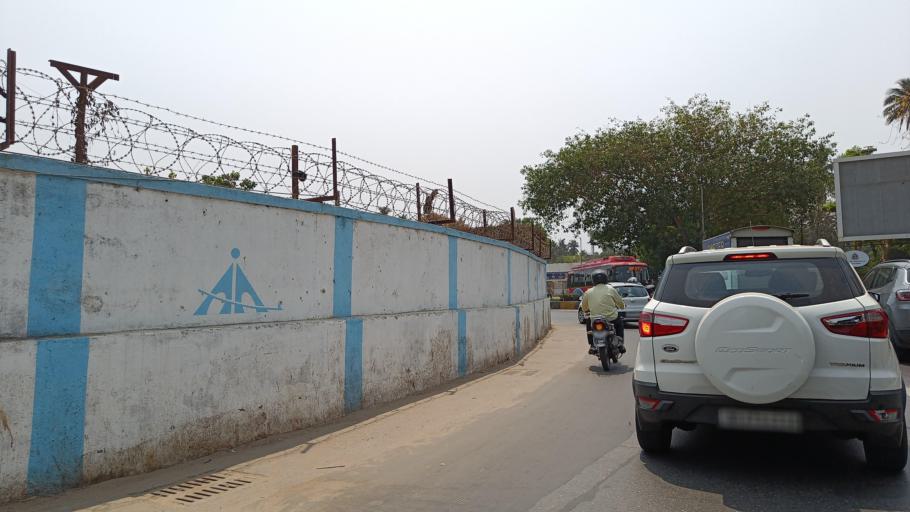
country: IN
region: Maharashtra
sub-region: Mumbai Suburban
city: Mumbai
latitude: 19.0967
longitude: 72.8271
